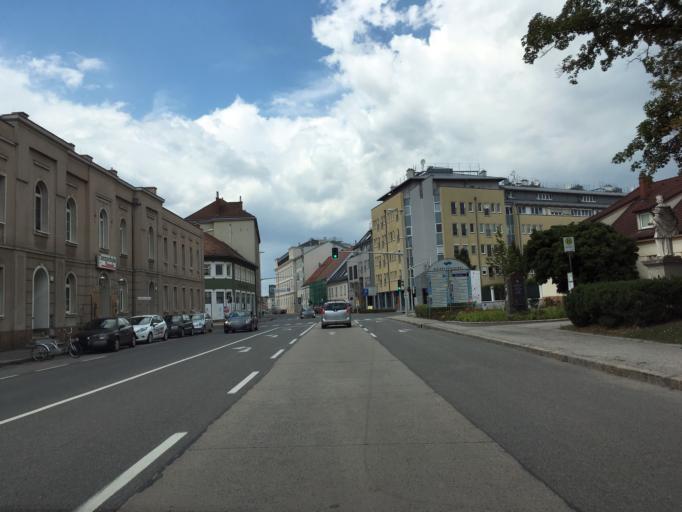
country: AT
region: Lower Austria
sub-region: Politischer Bezirk Korneuburg
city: Korneuburg
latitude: 48.3417
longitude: 16.3356
